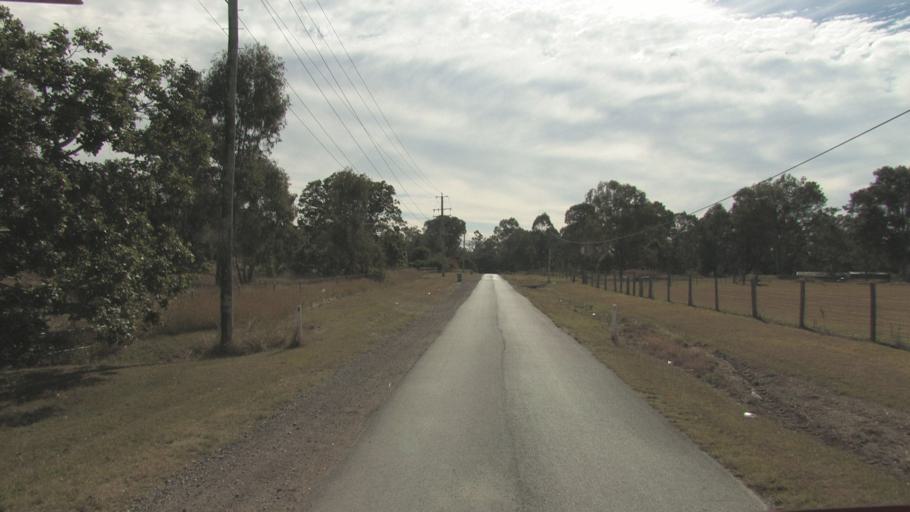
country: AU
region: Queensland
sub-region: Logan
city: North Maclean
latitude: -27.7775
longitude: 153.0082
